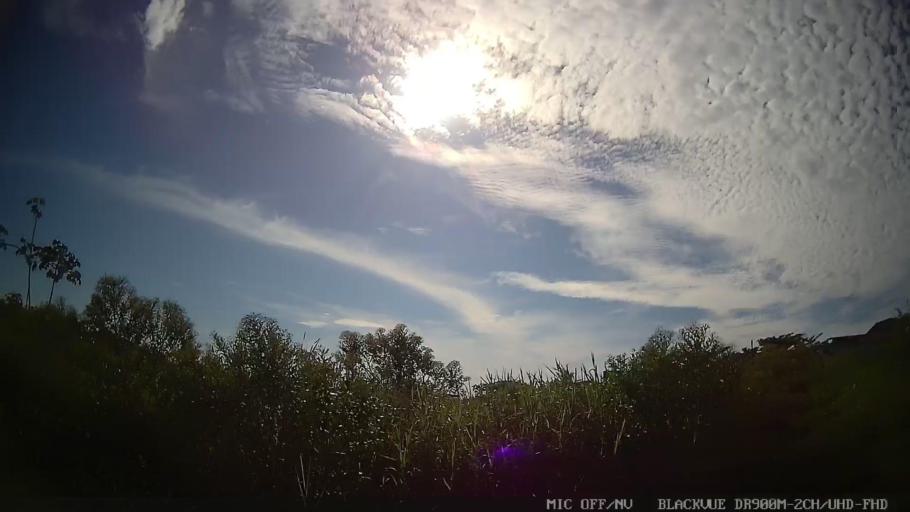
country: BR
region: Sao Paulo
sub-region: Iguape
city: Iguape
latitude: -24.7668
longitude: -47.5860
